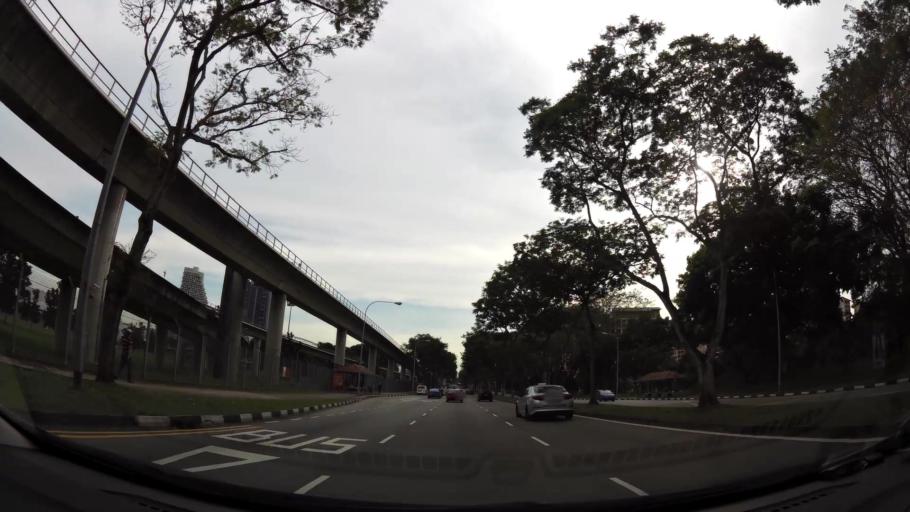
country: SG
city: Singapore
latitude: 1.3588
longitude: 103.8514
